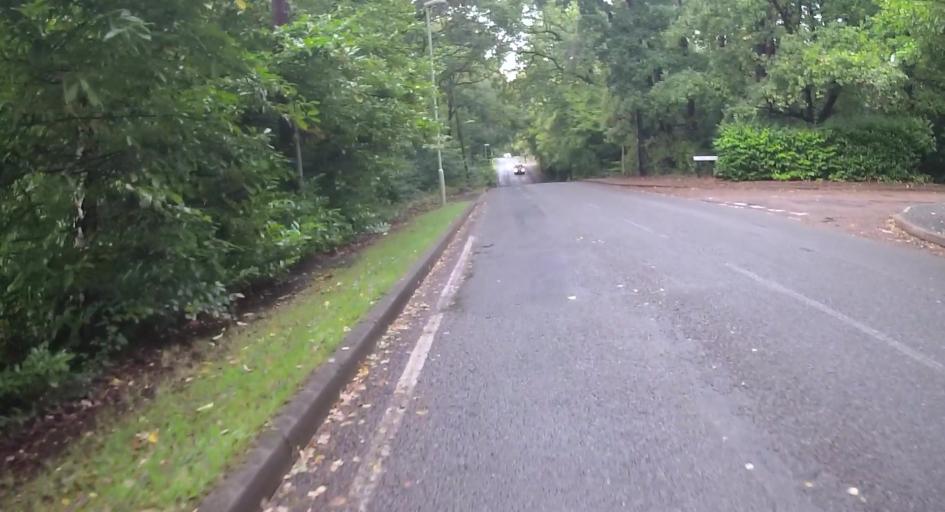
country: GB
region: England
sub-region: Hampshire
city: Tadley
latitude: 51.3549
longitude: -1.1714
